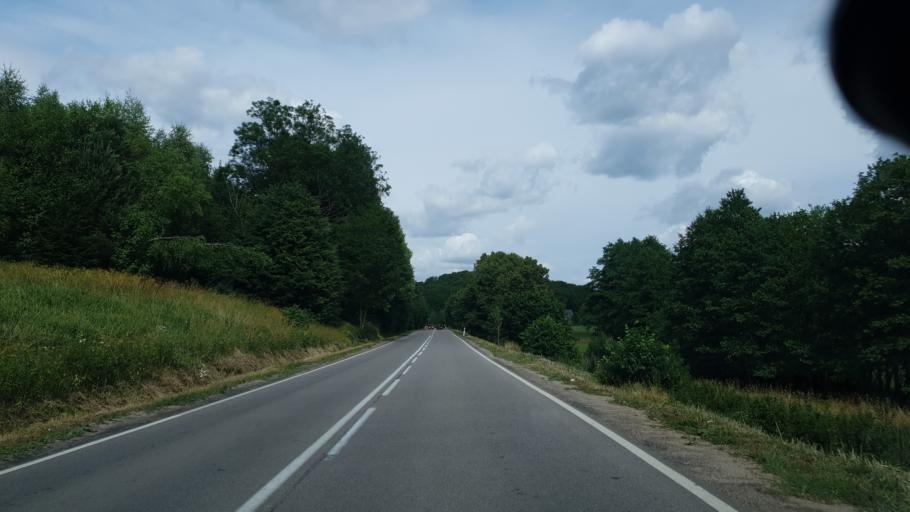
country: PL
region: Pomeranian Voivodeship
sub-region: Powiat kartuski
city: Kartuzy
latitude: 54.3110
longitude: 18.1545
